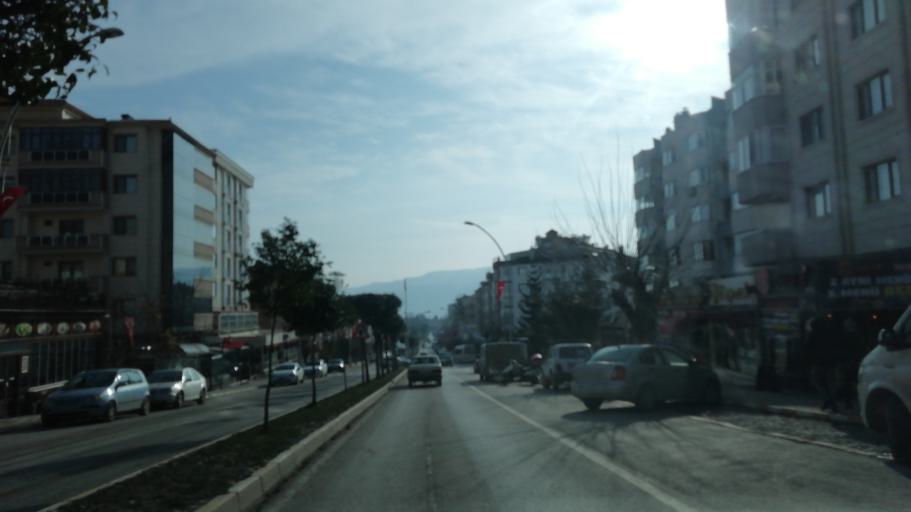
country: TR
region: Karabuk
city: Safranbolu
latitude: 41.2534
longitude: 32.6784
